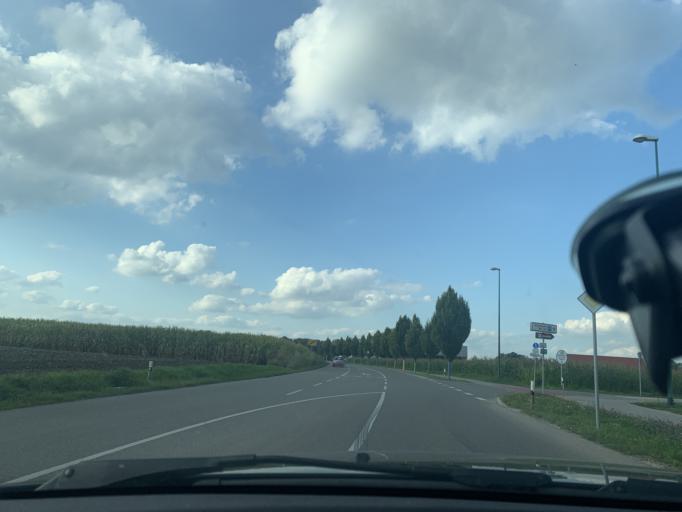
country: DE
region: Bavaria
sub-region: Swabia
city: Kissing
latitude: 48.3071
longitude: 10.9805
